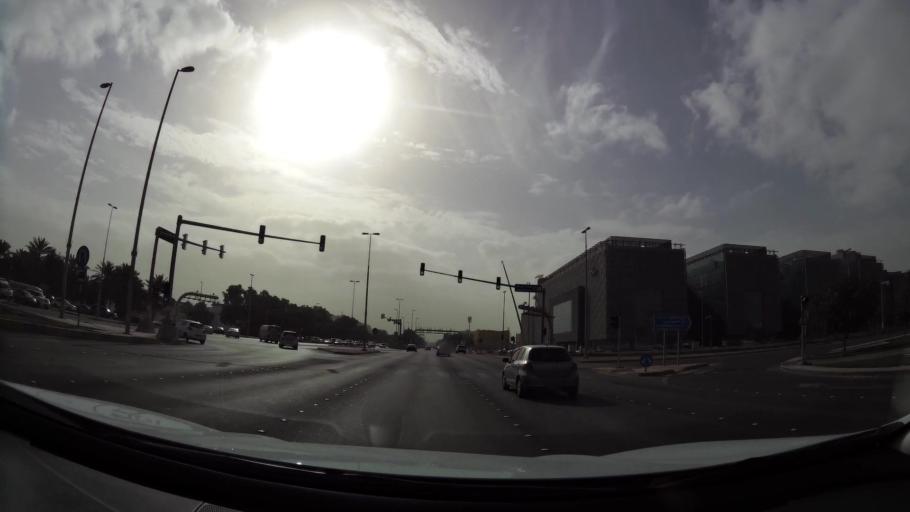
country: AE
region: Abu Dhabi
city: Abu Dhabi
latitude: 24.4511
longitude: 54.3967
